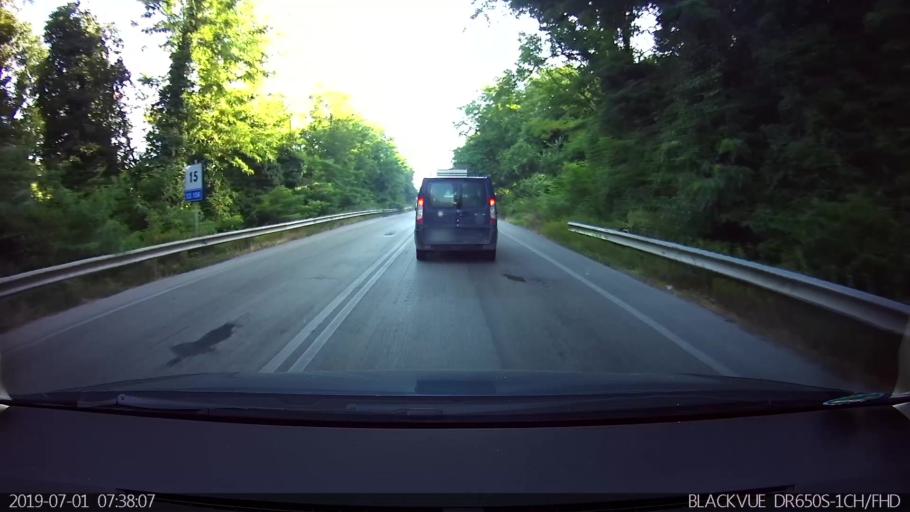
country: IT
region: Latium
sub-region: Provincia di Frosinone
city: Giuliano di Roma
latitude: 41.5421
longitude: 13.2681
